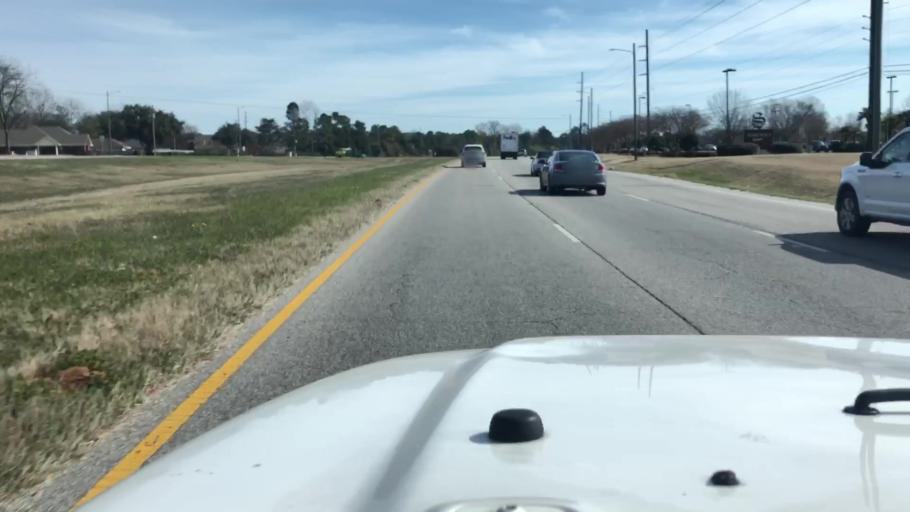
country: US
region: Alabama
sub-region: Elmore County
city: Blue Ridge
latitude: 32.3820
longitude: -86.1640
